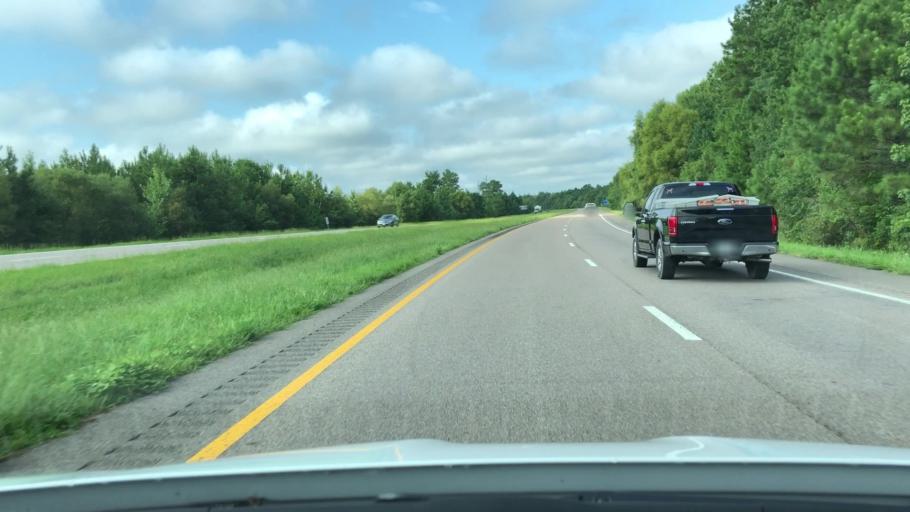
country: US
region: Virginia
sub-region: City of Portsmouth
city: Portsmouth Heights
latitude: 36.6746
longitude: -76.3492
